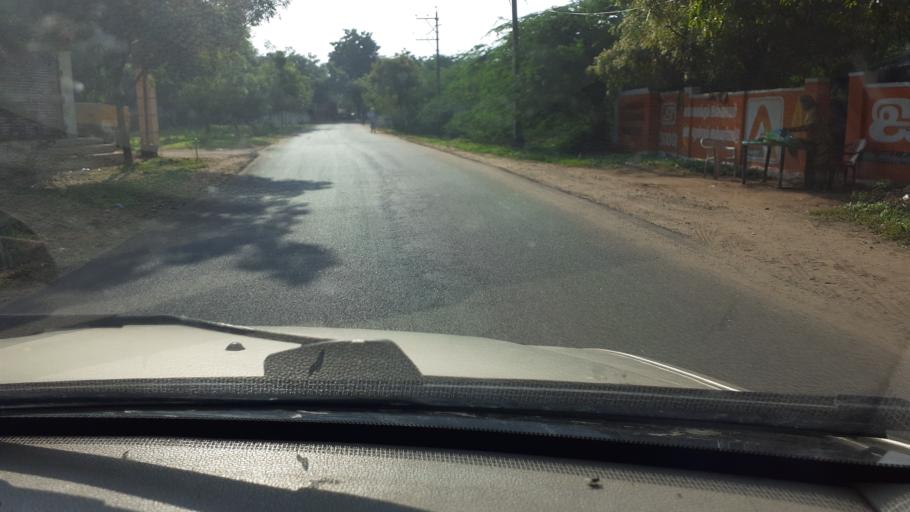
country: IN
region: Tamil Nadu
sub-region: Thoothukkudi
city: Eral
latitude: 8.5790
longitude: 78.0233
